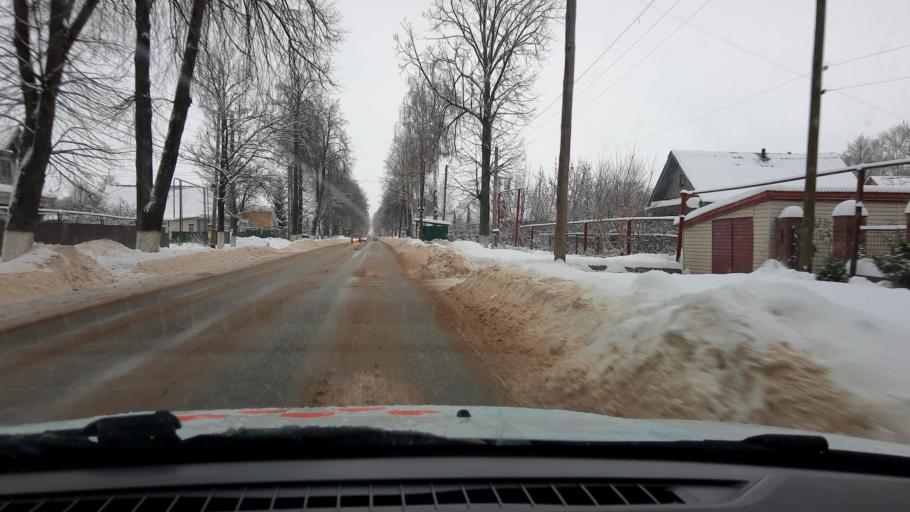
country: RU
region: Nizjnij Novgorod
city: Chkalovsk
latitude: 56.7632
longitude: 43.2449
